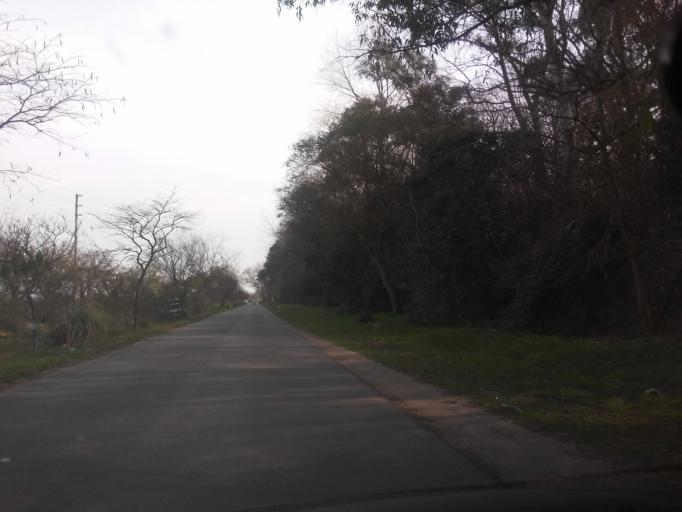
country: AR
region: Buenos Aires
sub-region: Partido de Marcos Paz
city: Marcos Paz
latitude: -34.6719
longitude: -58.8582
